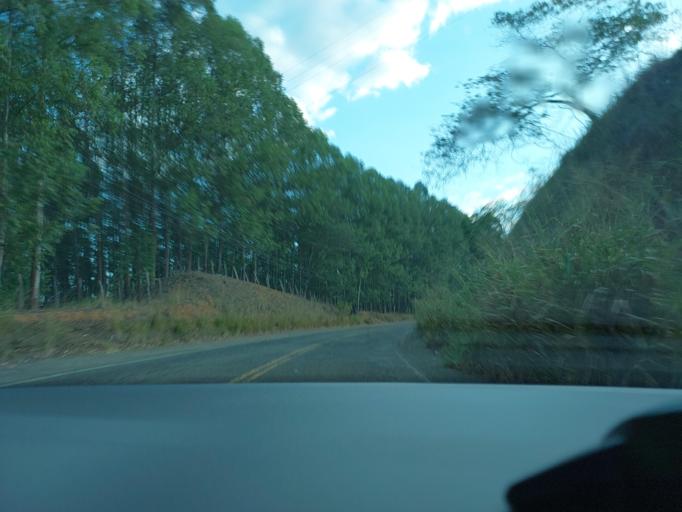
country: BR
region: Rio de Janeiro
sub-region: Natividade
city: Natividade
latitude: -21.1908
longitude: -42.1064
